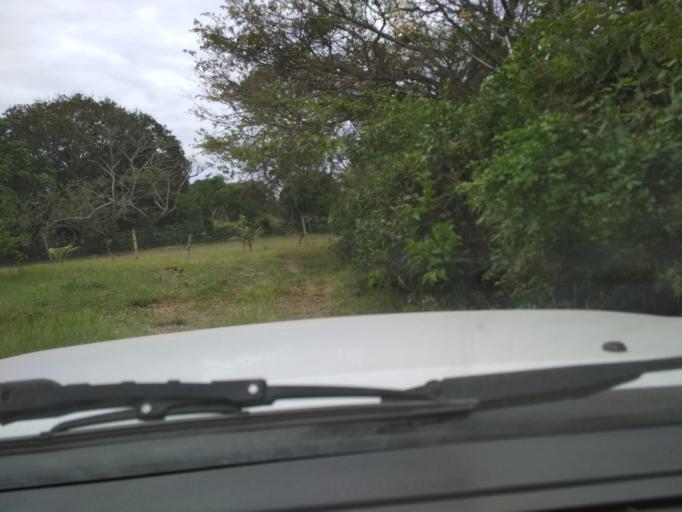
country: MX
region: Veracruz
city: El Tejar
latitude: 19.0724
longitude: -96.1418
